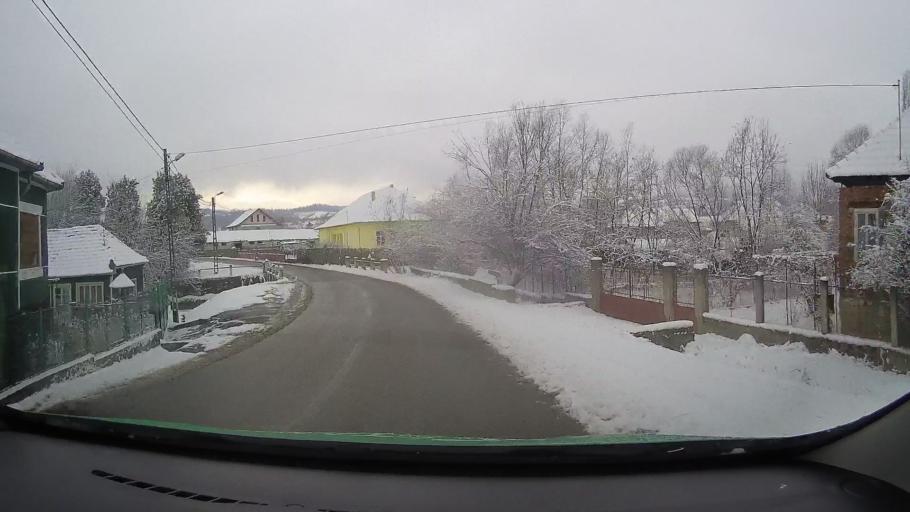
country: RO
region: Hunedoara
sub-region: Oras Hateg
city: Hateg
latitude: 45.6542
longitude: 22.9237
